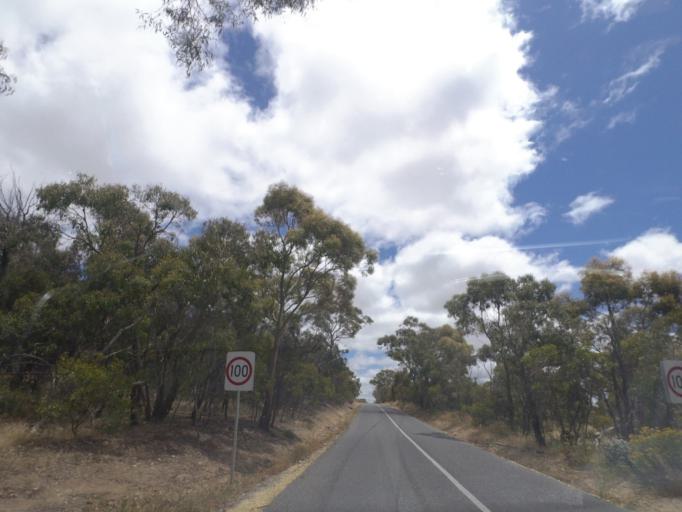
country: AU
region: Victoria
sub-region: Moorabool
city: Bacchus Marsh
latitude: -37.6597
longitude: 144.3227
